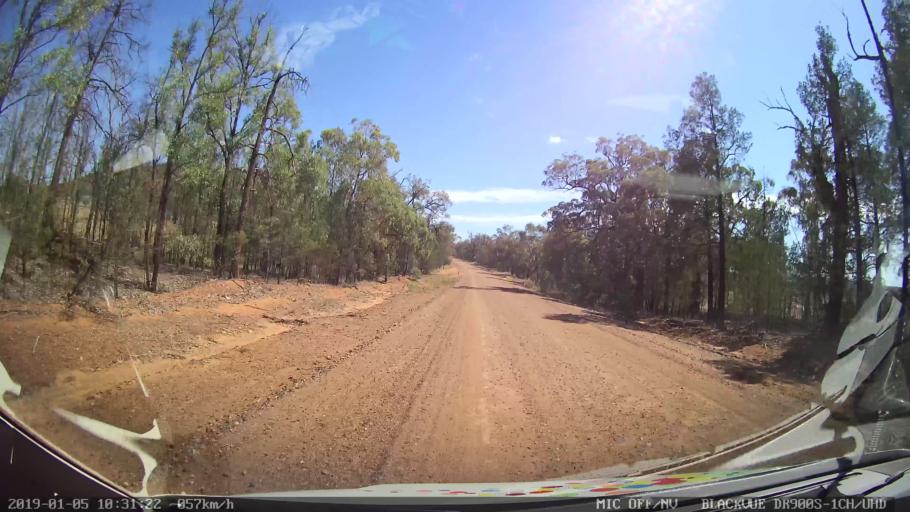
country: AU
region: New South Wales
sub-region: Gilgandra
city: Gilgandra
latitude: -31.5248
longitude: 148.9276
